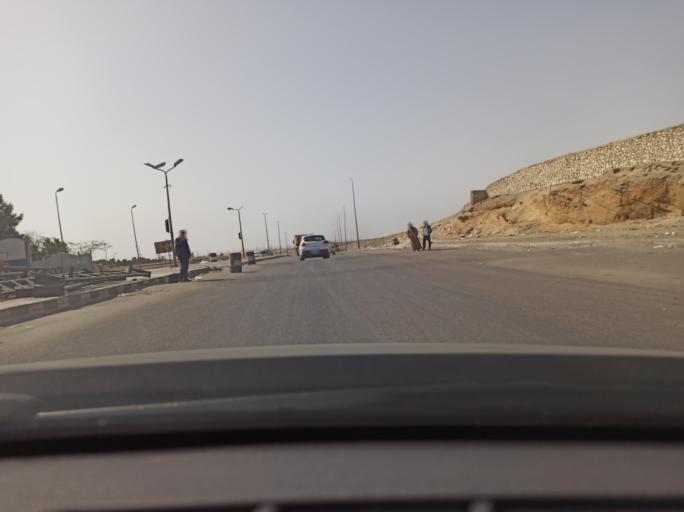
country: EG
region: Muhafazat al Qahirah
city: Halwan
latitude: 29.8196
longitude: 31.3523
